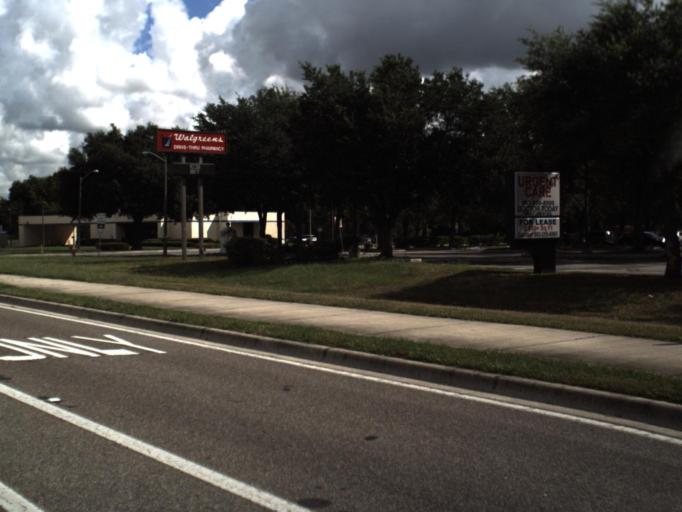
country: US
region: Florida
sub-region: Polk County
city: Gibsonia
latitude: 28.0995
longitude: -81.9736
